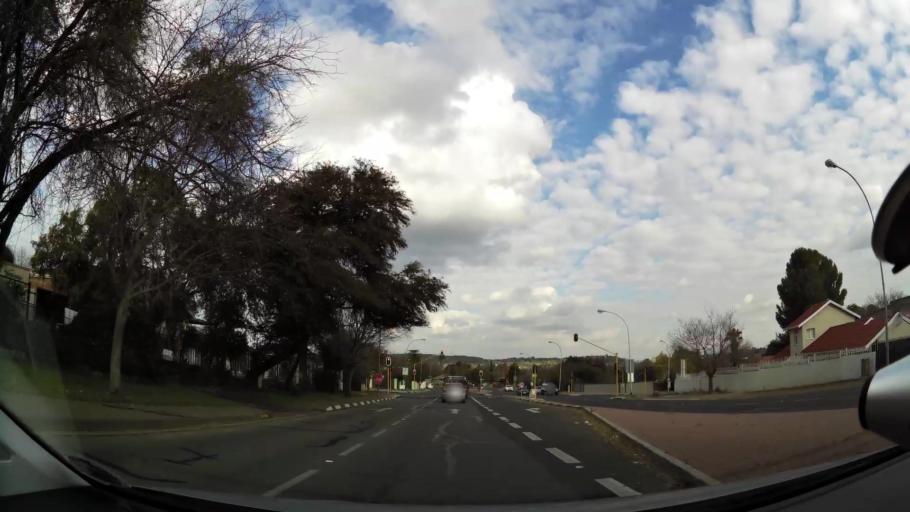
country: ZA
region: Orange Free State
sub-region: Mangaung Metropolitan Municipality
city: Bloemfontein
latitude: -29.0797
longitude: 26.2068
